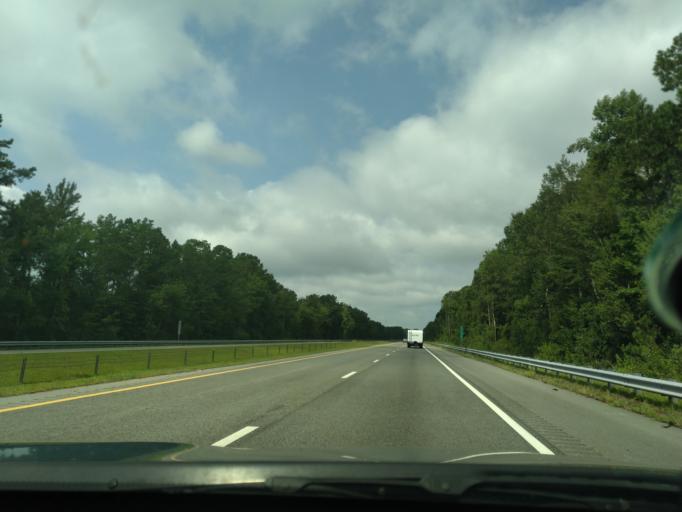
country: US
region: North Carolina
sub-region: Pitt County
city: Bethel
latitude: 35.8325
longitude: -77.3259
